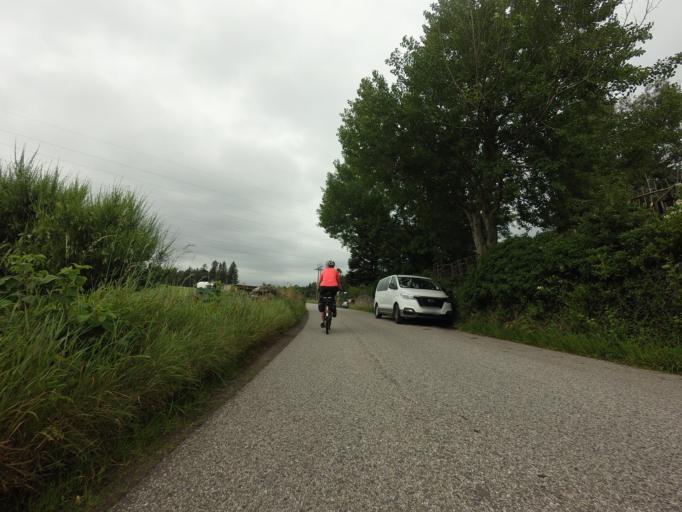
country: GB
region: Scotland
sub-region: Highland
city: Evanton
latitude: 57.8861
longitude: -4.3821
